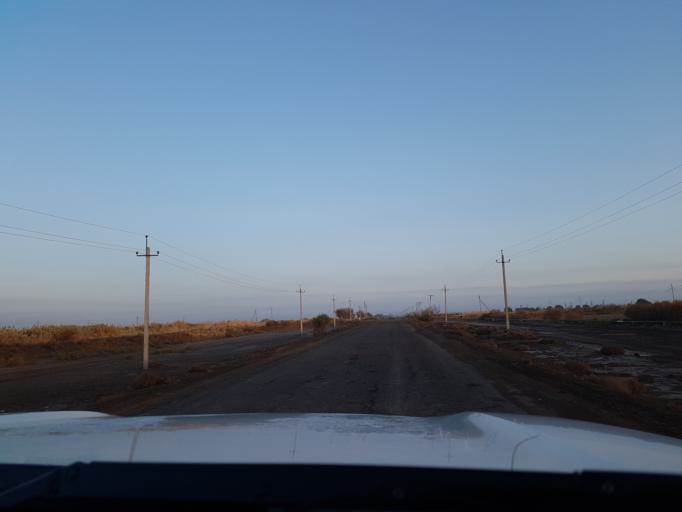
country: TM
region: Dasoguz
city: Koeneuergench
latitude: 41.8409
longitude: 58.7045
